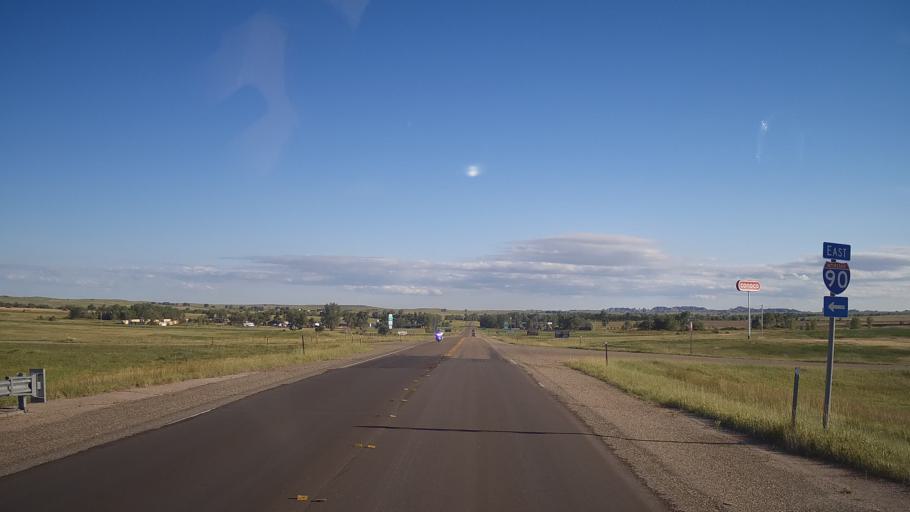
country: US
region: South Dakota
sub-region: Haakon County
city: Philip
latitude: 43.8396
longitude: -101.9004
